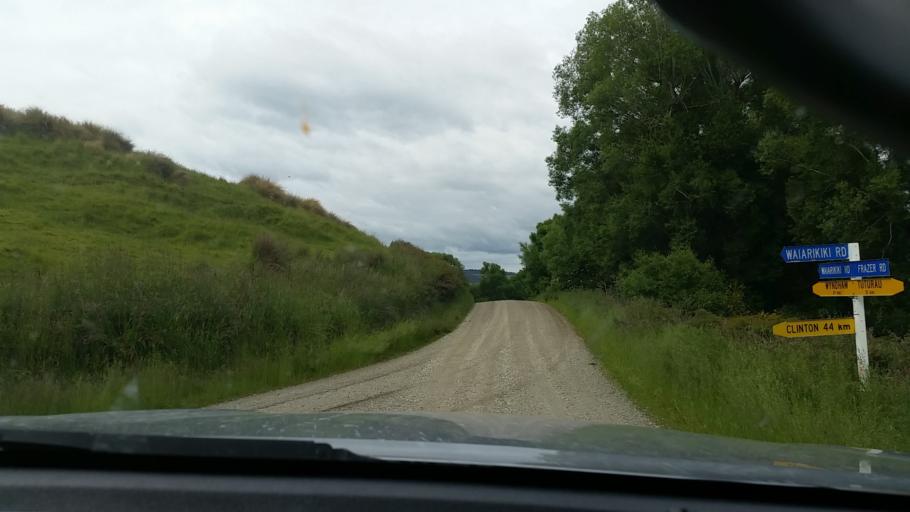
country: NZ
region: Southland
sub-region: Gore District
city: Gore
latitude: -46.2649
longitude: 168.9975
